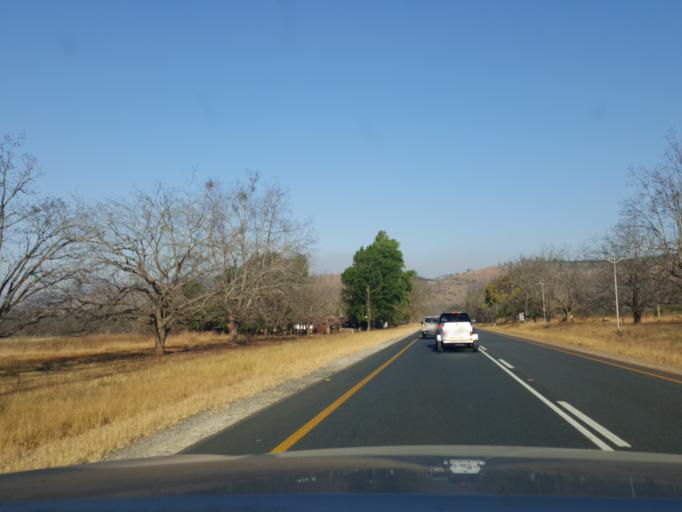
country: ZA
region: Mpumalanga
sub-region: Ehlanzeni District
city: Nelspruit
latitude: -25.4450
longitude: 30.6565
